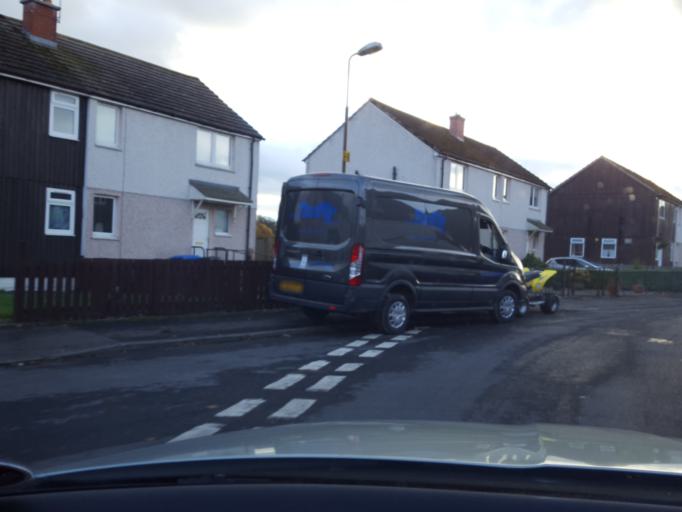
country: GB
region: Scotland
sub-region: West Lothian
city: West Calder
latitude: 55.8586
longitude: -3.5496
